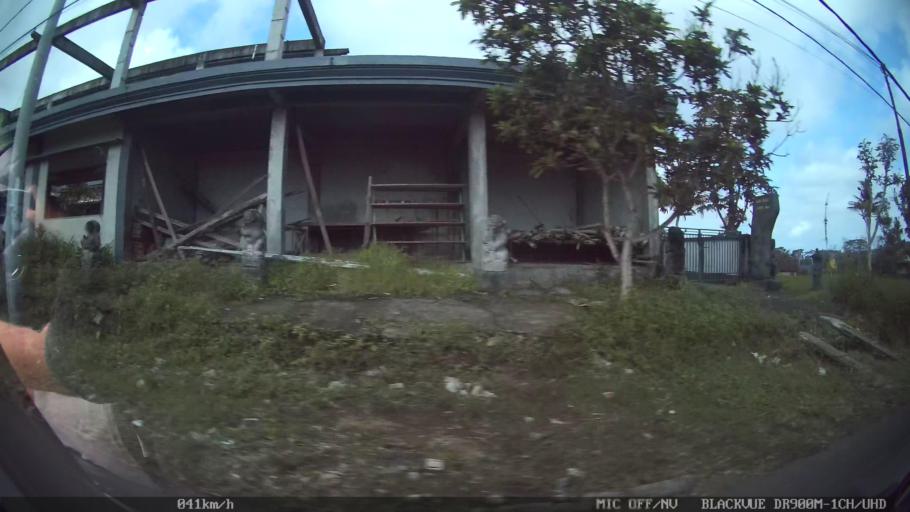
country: ID
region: Bali
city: Banjar Pesalakan
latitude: -8.4980
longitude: 115.3045
